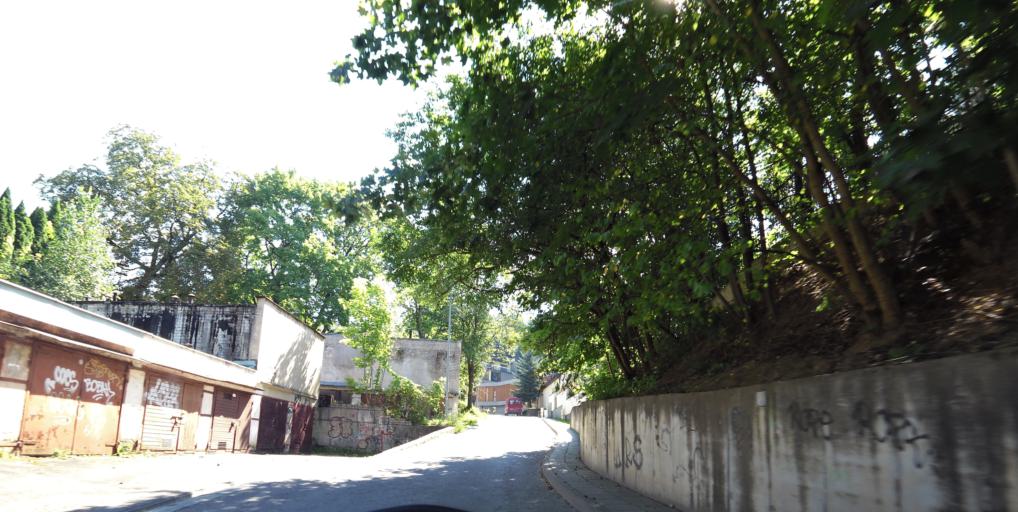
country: LT
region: Vilnius County
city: Rasos
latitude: 54.6917
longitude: 25.3130
